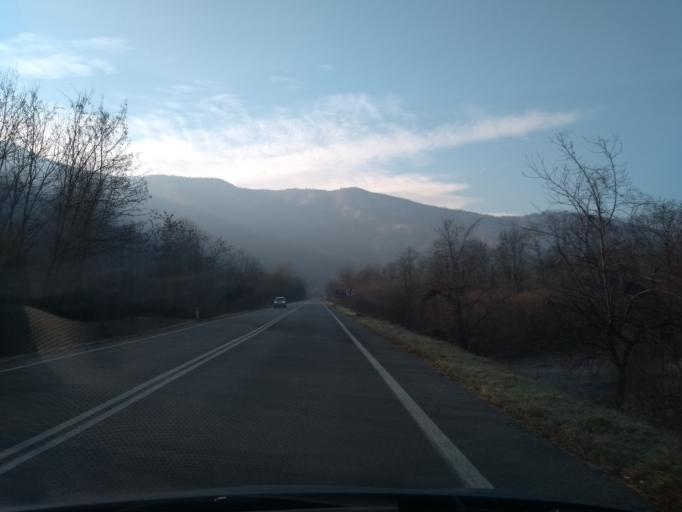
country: IT
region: Piedmont
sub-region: Provincia di Torino
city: Germagnano
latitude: 45.2637
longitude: 7.4767
